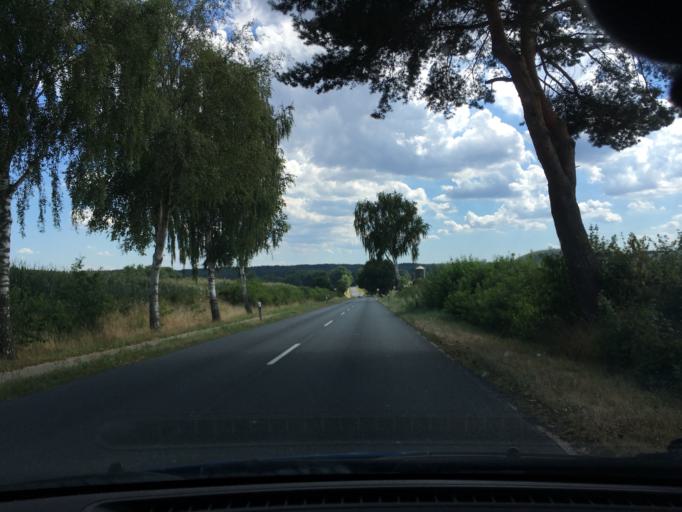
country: DE
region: Lower Saxony
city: Amelinghausen
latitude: 53.1161
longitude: 10.2170
